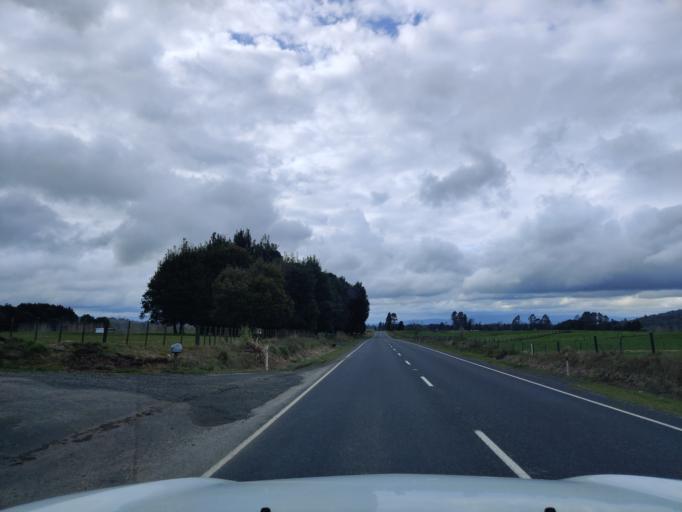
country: NZ
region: Waikato
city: Turangi
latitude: -39.0404
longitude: 175.3832
